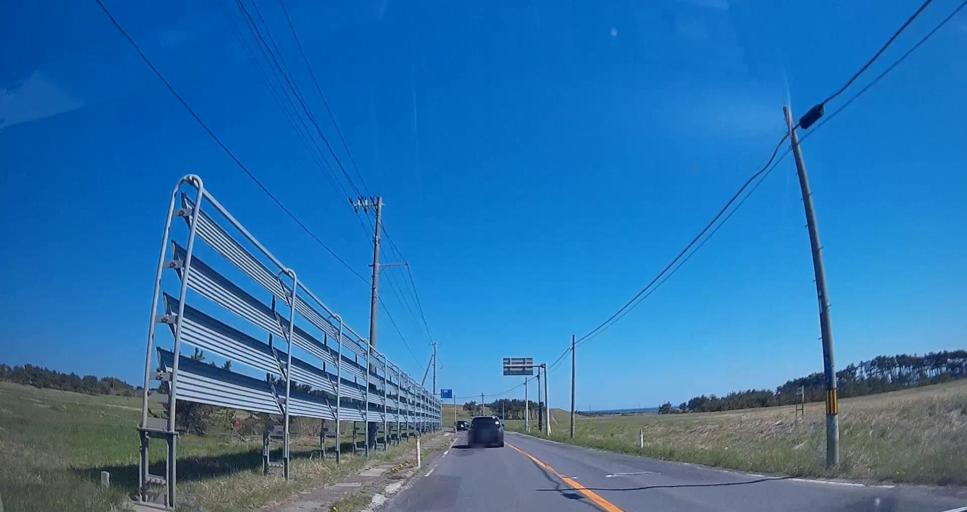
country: JP
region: Aomori
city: Misawa
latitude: 40.6951
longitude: 141.4239
